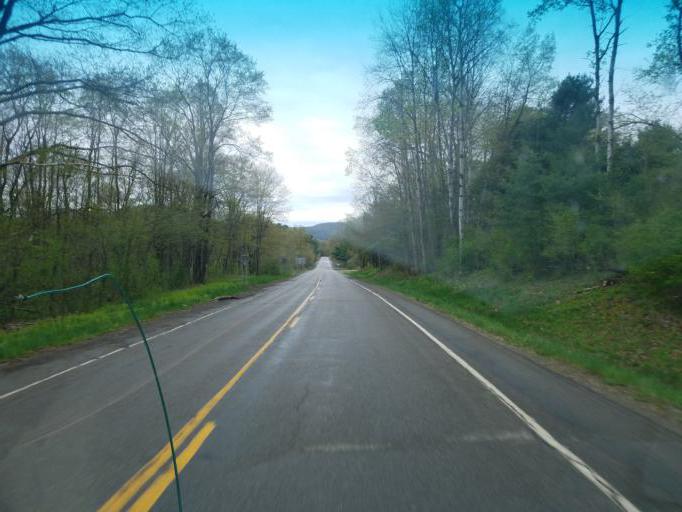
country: US
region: New York
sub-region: Allegany County
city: Wellsville
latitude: 41.9998
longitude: -77.8619
